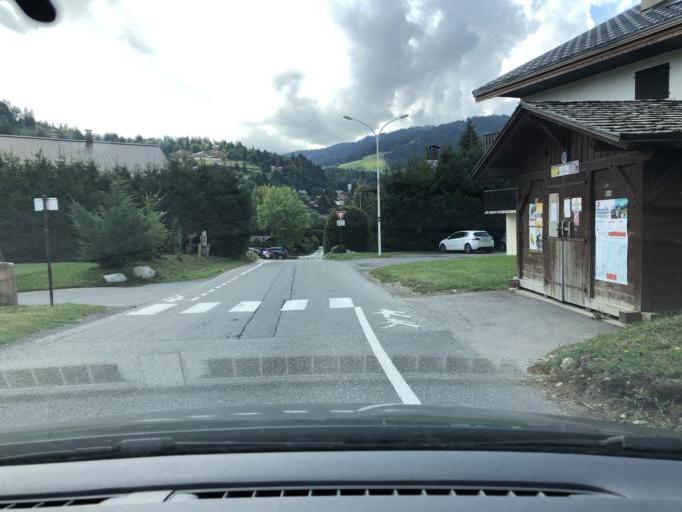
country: FR
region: Rhone-Alpes
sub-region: Departement de la Haute-Savoie
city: Megeve
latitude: 45.8667
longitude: 6.6245
